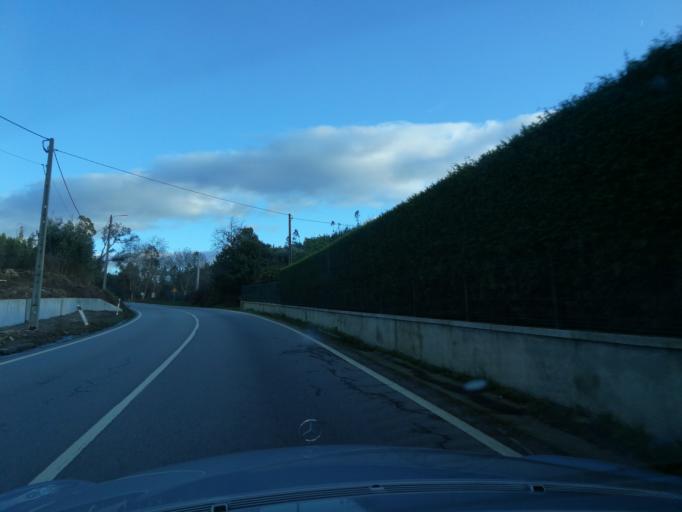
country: PT
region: Braga
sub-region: Barcelos
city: Vila Frescainha
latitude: 41.5699
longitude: -8.6849
